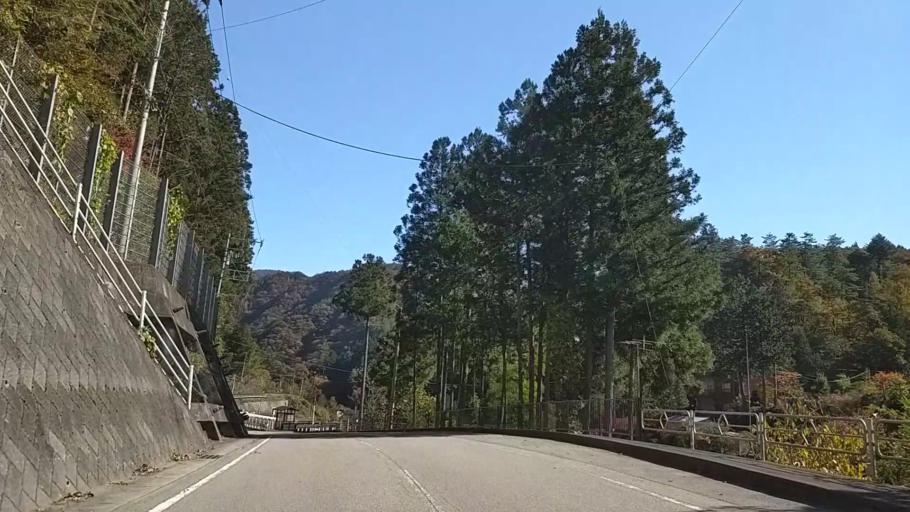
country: JP
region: Yamanashi
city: Otsuki
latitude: 35.7590
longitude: 138.9468
